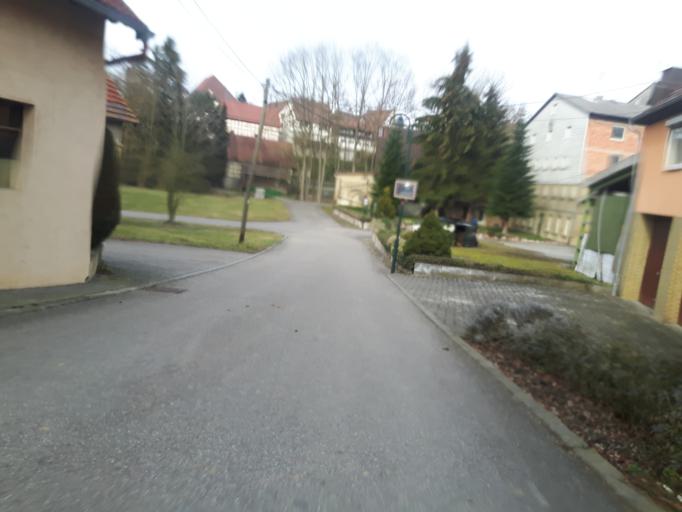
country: DE
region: Baden-Wuerttemberg
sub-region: Regierungsbezirk Stuttgart
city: Bretzfeld
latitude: 49.2013
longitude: 9.4309
